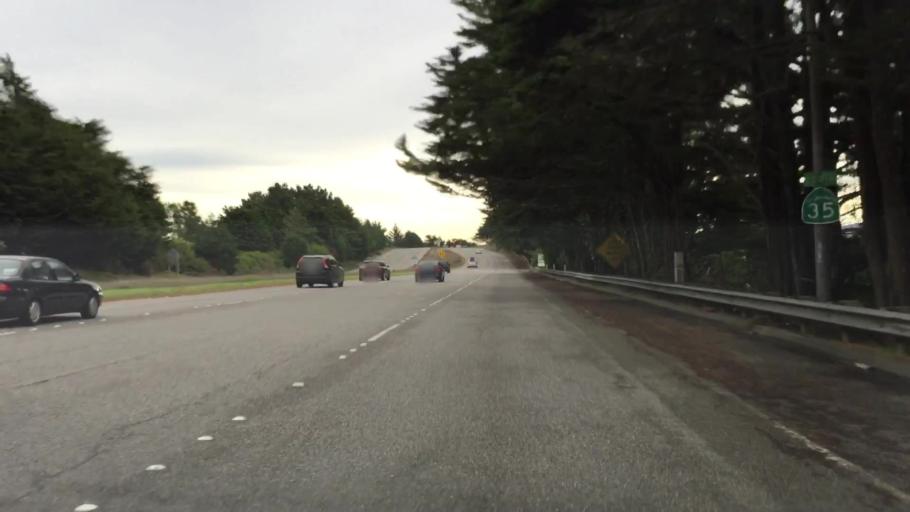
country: US
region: California
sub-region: San Mateo County
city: Broadmoor
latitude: 37.6653
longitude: -122.4807
